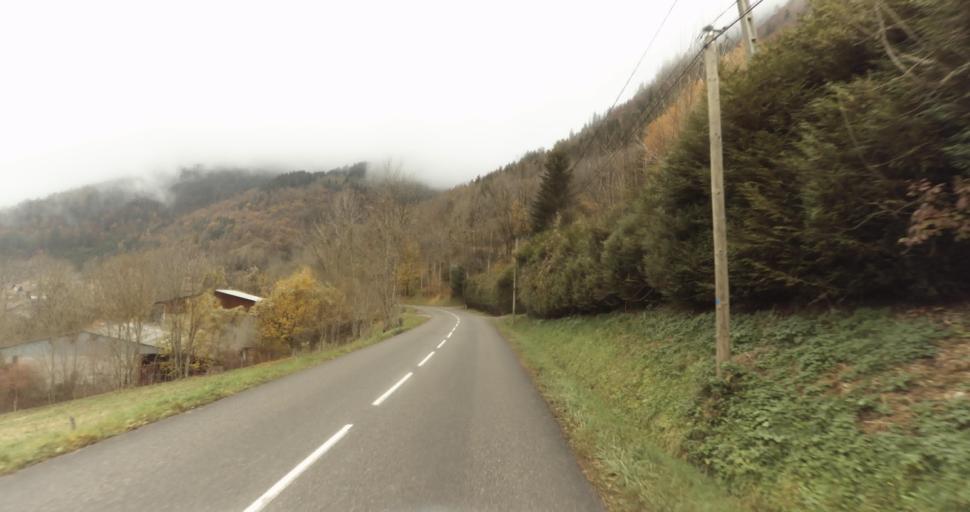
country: FR
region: Rhone-Alpes
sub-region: Departement de la Haute-Savoie
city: Thorens-Glieres
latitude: 45.9809
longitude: 6.2831
